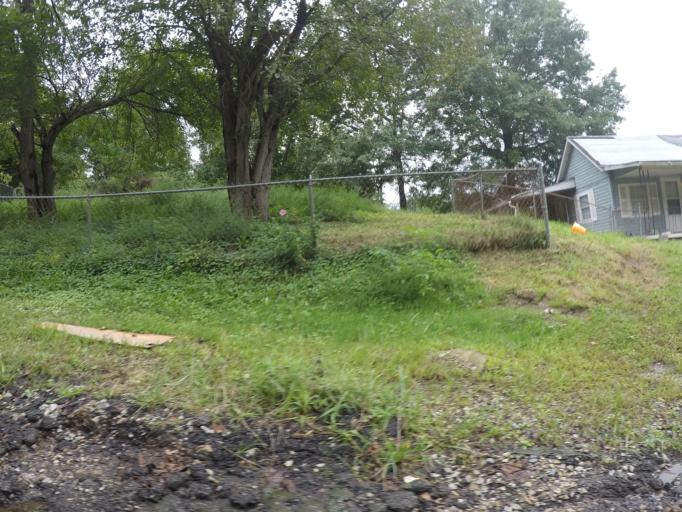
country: US
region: West Virginia
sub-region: Cabell County
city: Pea Ridge
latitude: 38.4291
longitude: -82.3724
